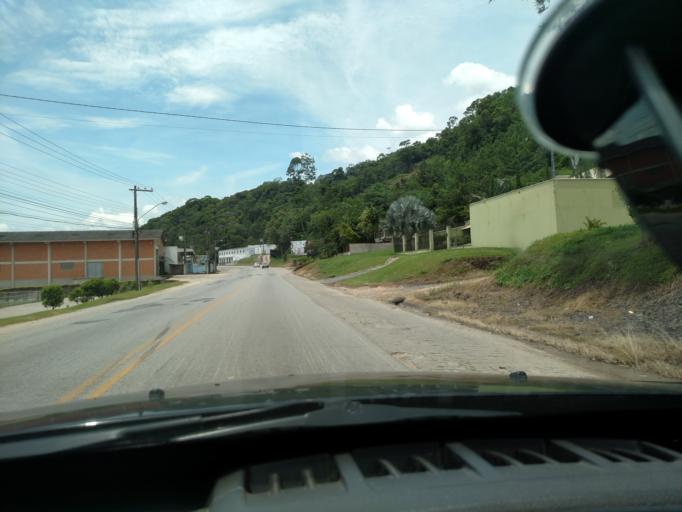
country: BR
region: Santa Catarina
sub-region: Gaspar
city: Gaspar
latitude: -26.9028
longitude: -48.9906
